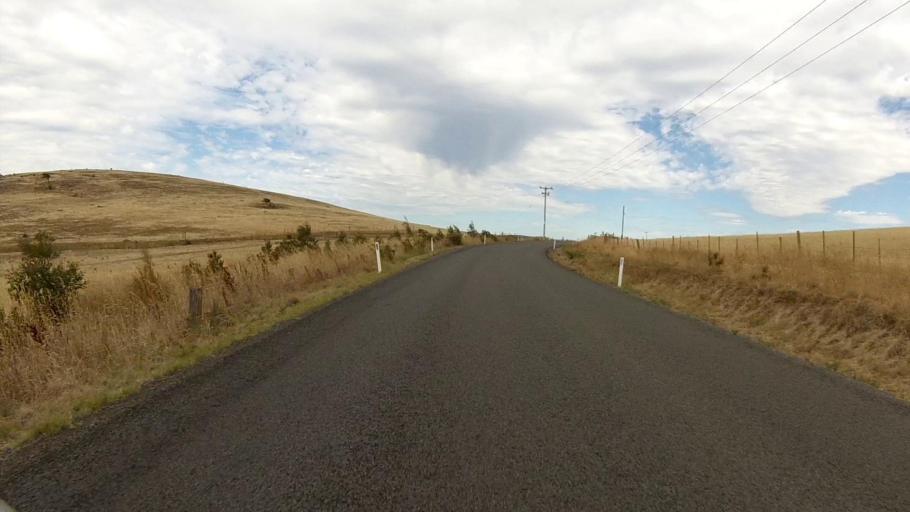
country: AU
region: Tasmania
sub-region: Sorell
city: Sorell
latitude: -42.8987
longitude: 147.7678
